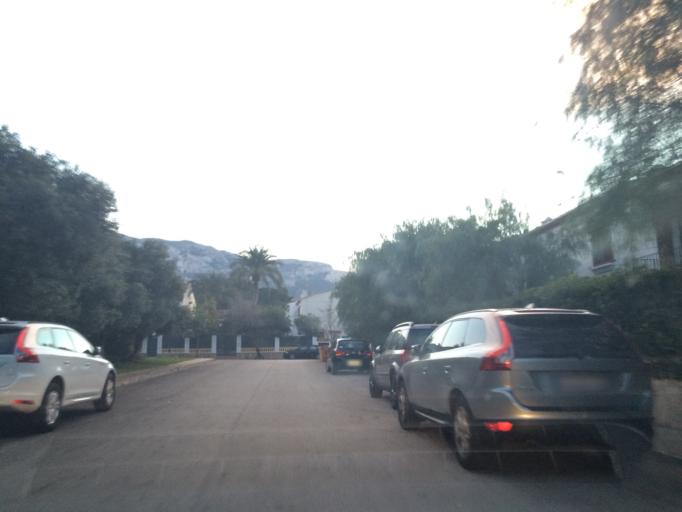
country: ES
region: Valencia
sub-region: Provincia de Alicante
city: Denia
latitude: 38.8332
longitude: 0.1196
